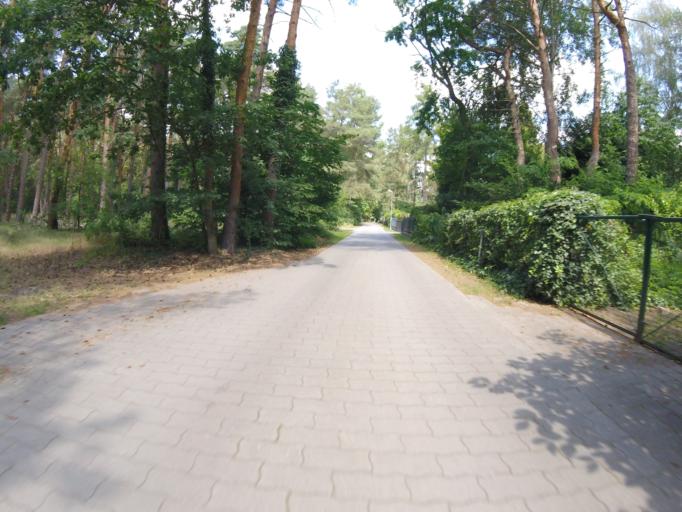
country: DE
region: Brandenburg
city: Bestensee
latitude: 52.2536
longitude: 13.6456
